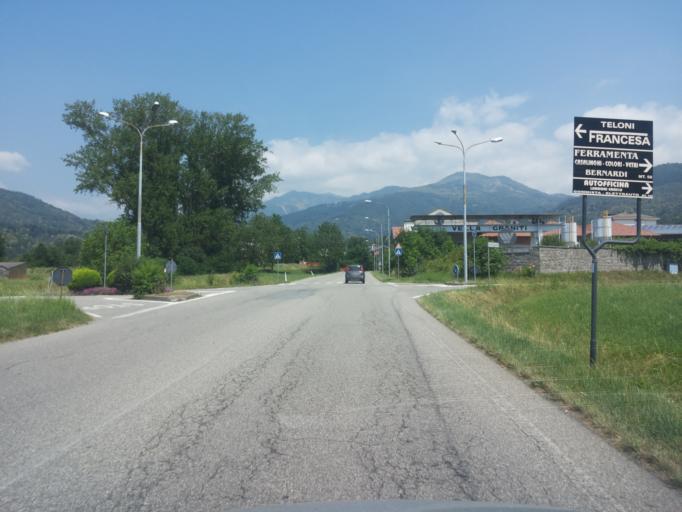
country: IT
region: Piedmont
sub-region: Provincia di Biella
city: Andorno Cacciorna
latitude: 45.6063
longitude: 8.0539
